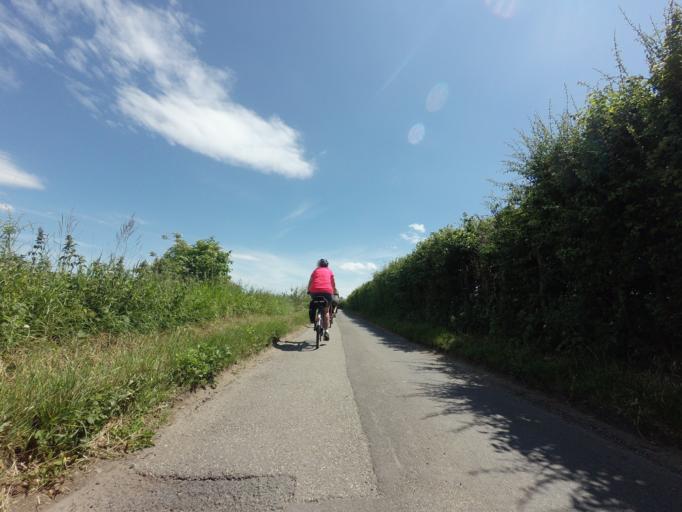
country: GB
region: England
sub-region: Kent
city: Cliffe
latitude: 51.4611
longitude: 0.5103
